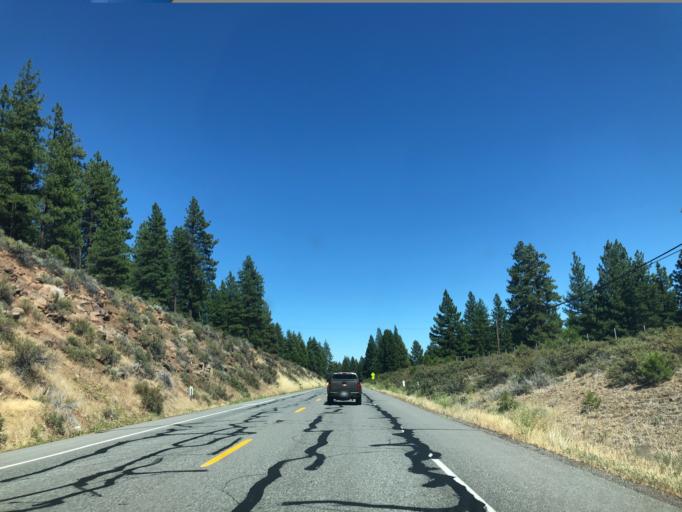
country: US
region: California
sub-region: Lassen County
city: Susanville
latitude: 40.4149
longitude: -120.7316
